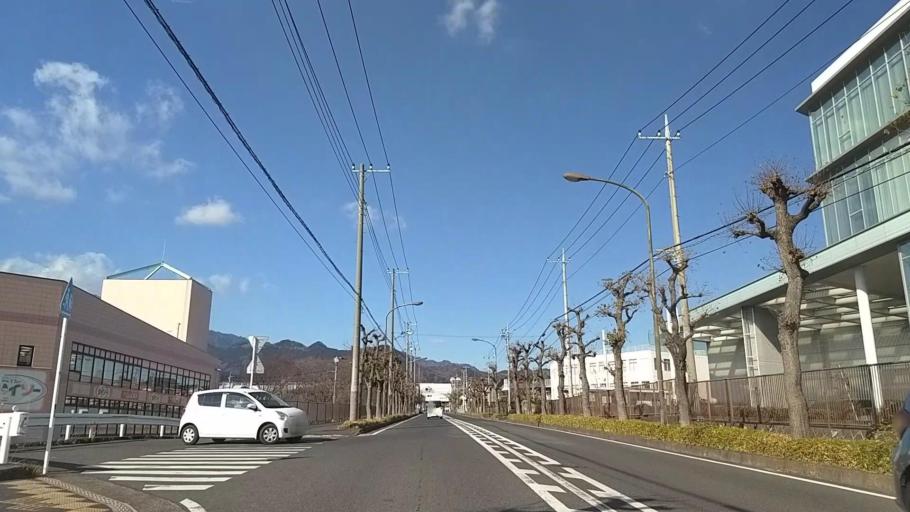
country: JP
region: Kanagawa
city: Isehara
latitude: 35.4029
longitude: 139.2963
